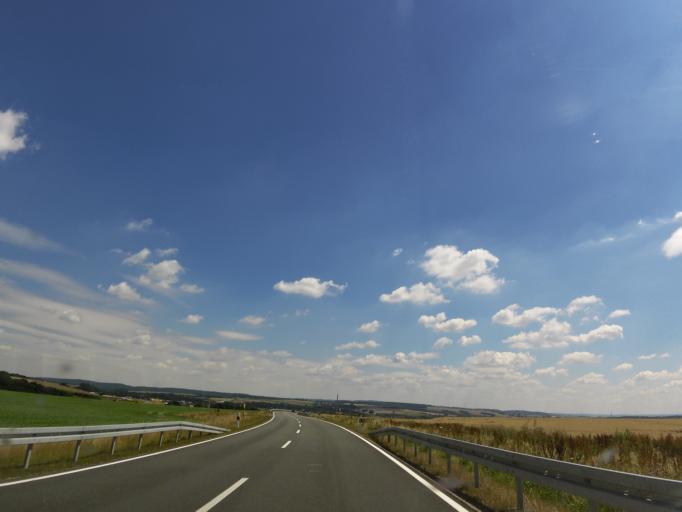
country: DE
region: Saxony
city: Pfaffroda
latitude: 50.8388
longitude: 12.5077
